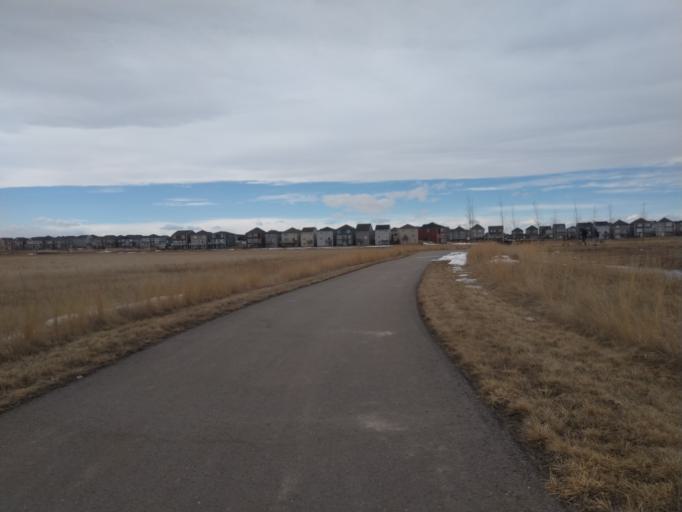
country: CA
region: Alberta
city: Calgary
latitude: 51.1490
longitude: -113.9564
